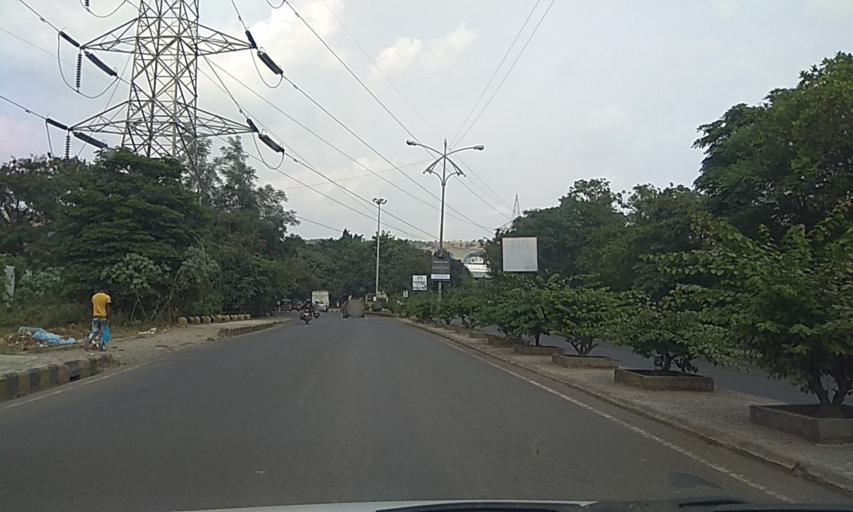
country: IN
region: Maharashtra
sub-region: Pune Division
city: Pimpri
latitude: 18.5927
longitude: 73.7076
